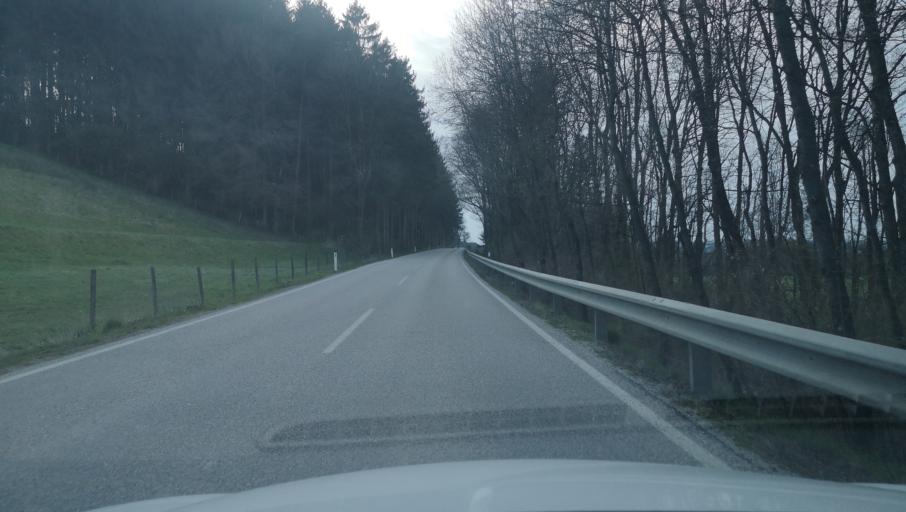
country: AT
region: Lower Austria
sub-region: Politischer Bezirk Amstetten
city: Amstetten
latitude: 48.1007
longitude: 14.8982
